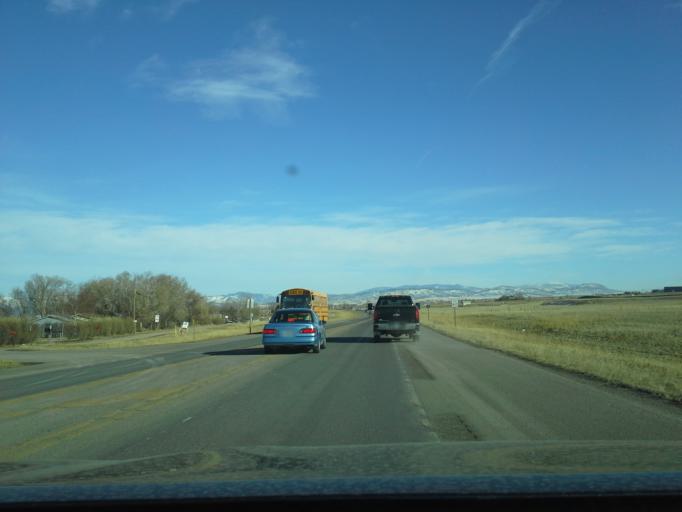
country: US
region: Montana
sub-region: Lewis and Clark County
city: Helena
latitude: 46.6166
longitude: -111.9891
